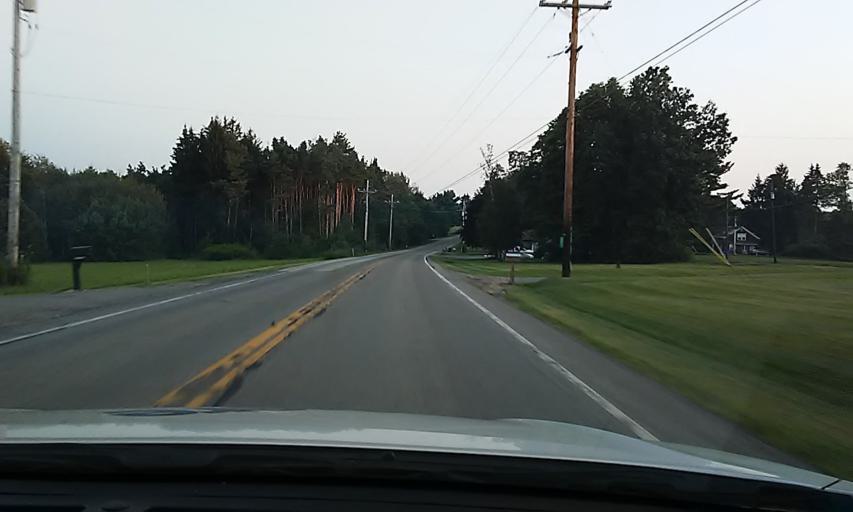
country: US
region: Pennsylvania
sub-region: Clarion County
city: Marianne
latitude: 41.2648
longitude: -79.3914
